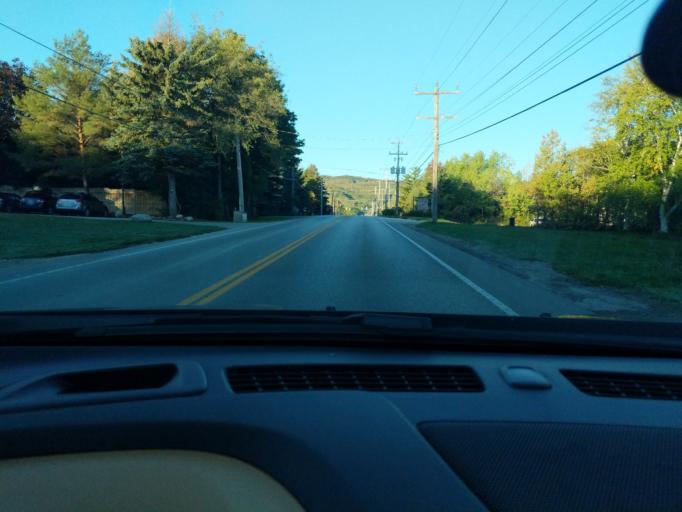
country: CA
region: Ontario
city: Collingwood
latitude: 44.4987
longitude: -80.2822
